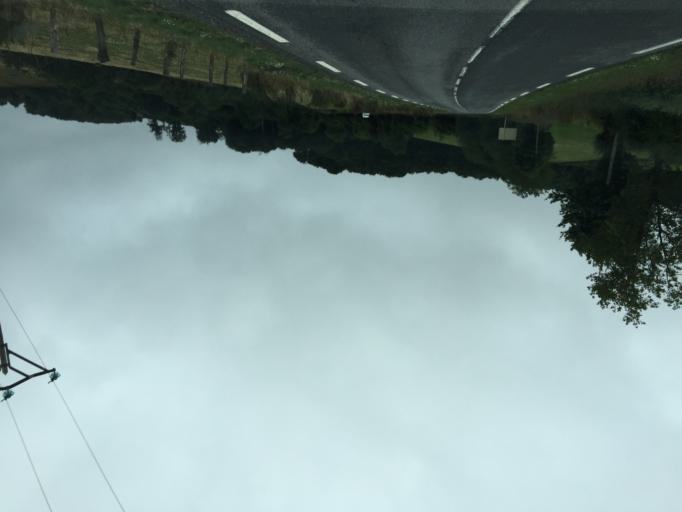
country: FR
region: Midi-Pyrenees
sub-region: Departement de l'Aveyron
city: Salles-Curan
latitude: 44.2413
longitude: 2.9023
